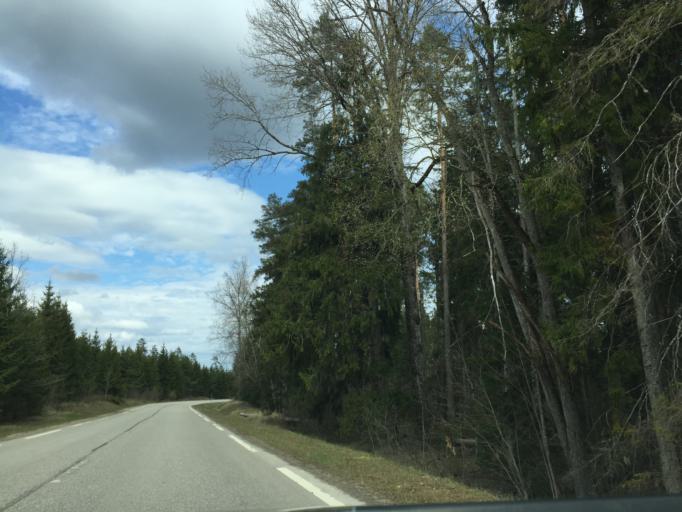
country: LV
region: Jaunpiebalga
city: Jaunpiebalga
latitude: 57.2341
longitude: 26.2476
